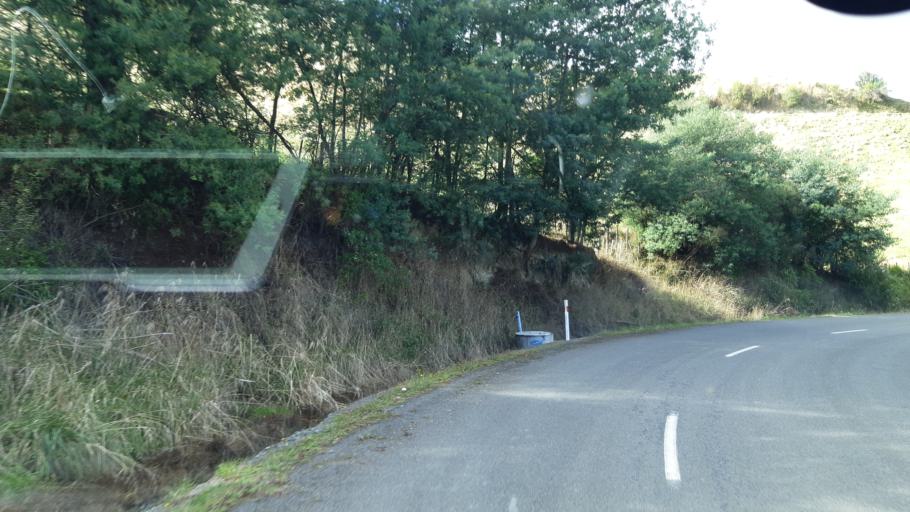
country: NZ
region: Manawatu-Wanganui
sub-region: Ruapehu District
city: Waiouru
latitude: -39.7422
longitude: 175.6653
